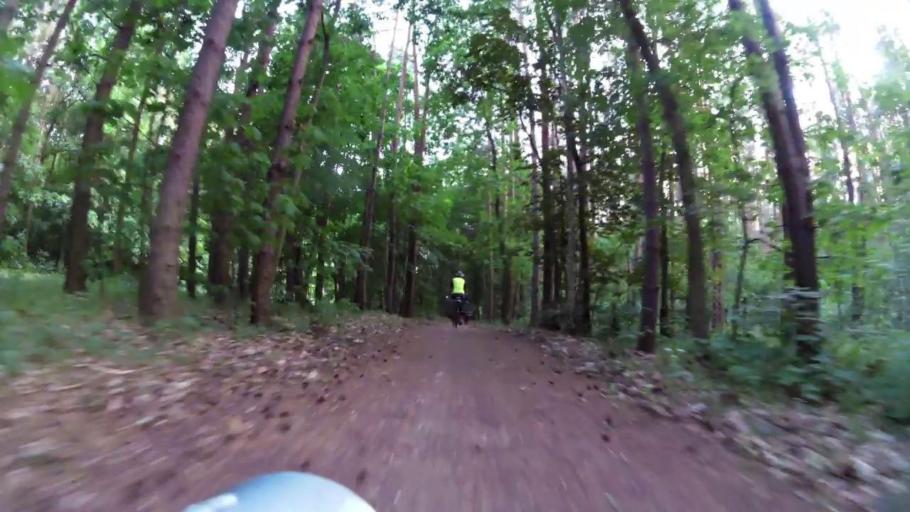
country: PL
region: Kujawsko-Pomorskie
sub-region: Powiat bydgoski
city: Dabrowa Chelminska
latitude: 53.1729
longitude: 18.2693
